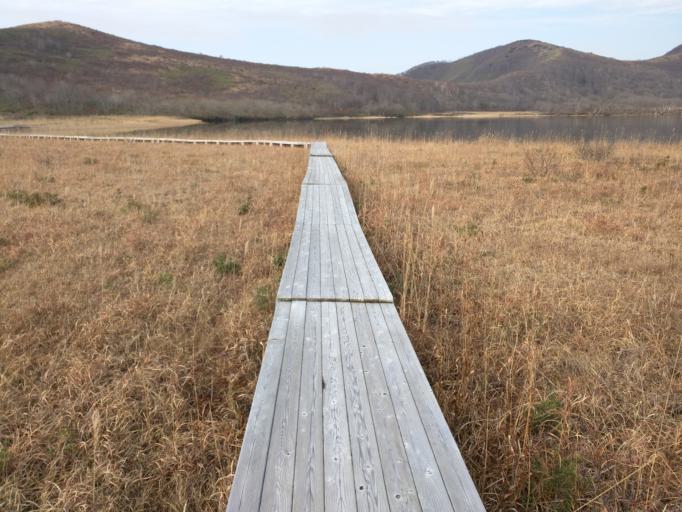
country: JP
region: Fukushima
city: Inawashiro
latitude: 37.6177
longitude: 140.0009
